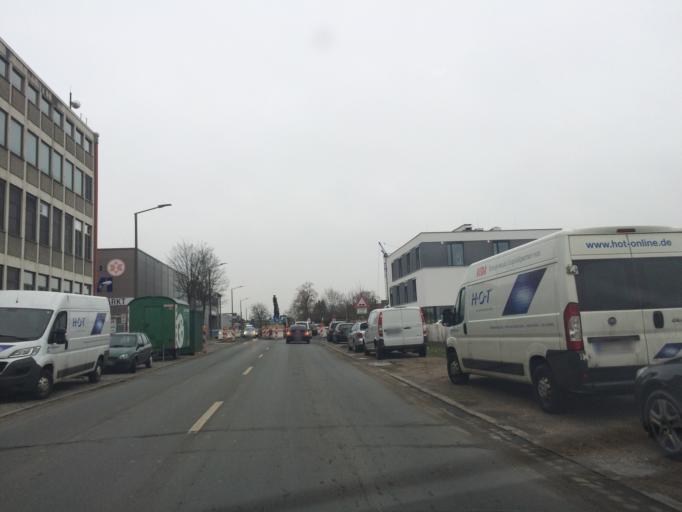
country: DE
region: Bavaria
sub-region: Regierungsbezirk Mittelfranken
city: Nuernberg
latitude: 49.4739
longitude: 11.0752
